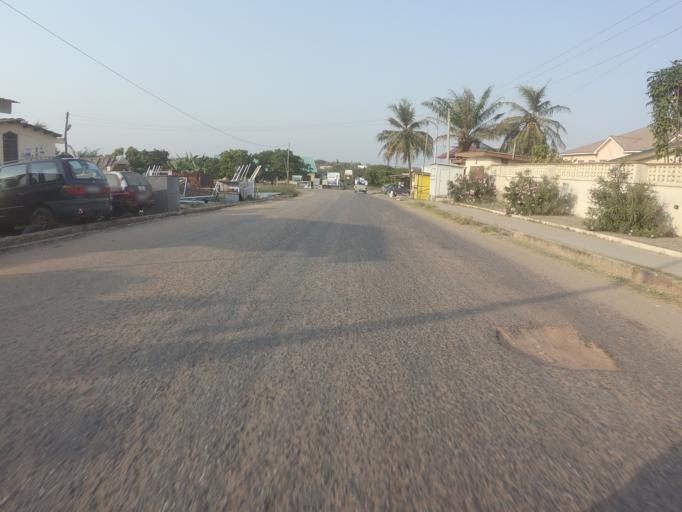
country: GH
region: Greater Accra
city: Nungua
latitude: 5.6162
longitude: -0.0477
